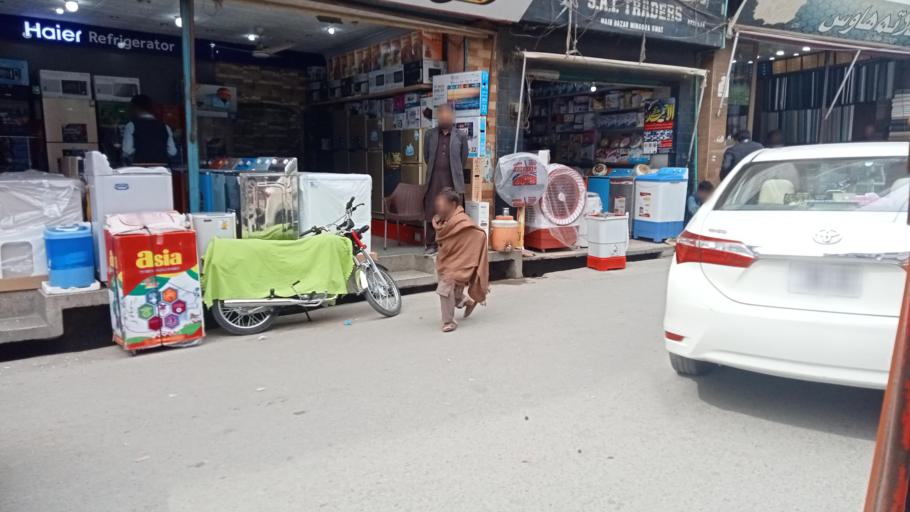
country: PK
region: Khyber Pakhtunkhwa
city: Mingora
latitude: 34.7741
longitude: 72.3603
